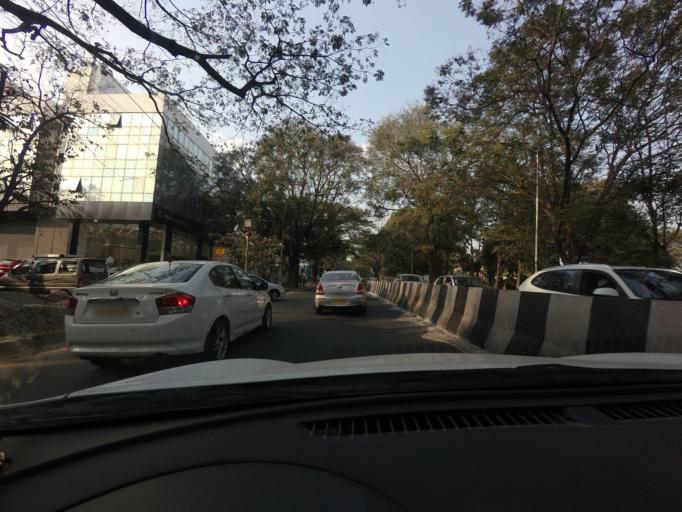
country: IN
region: Karnataka
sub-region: Bangalore Urban
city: Bangalore
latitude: 13.0047
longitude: 77.5840
